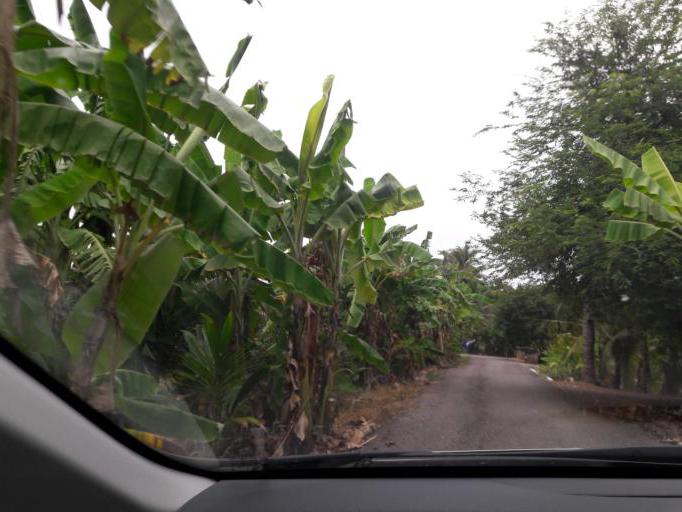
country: TH
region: Samut Sakhon
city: Ban Phaeo
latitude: 13.5917
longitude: 100.0291
